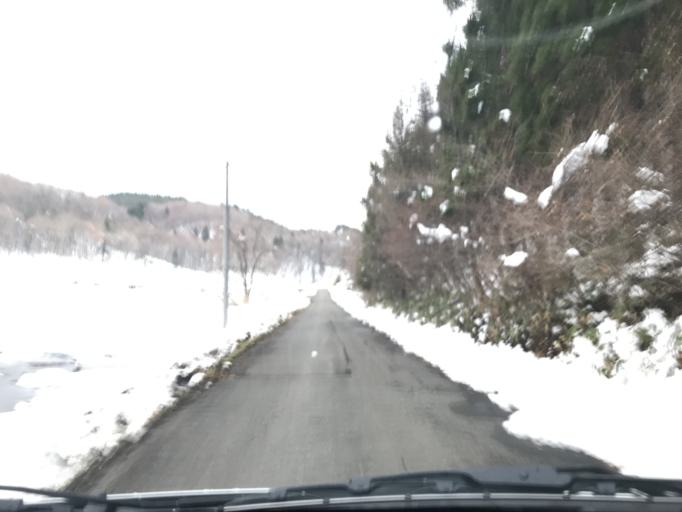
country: JP
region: Iwate
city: Mizusawa
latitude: 39.0428
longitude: 141.0113
